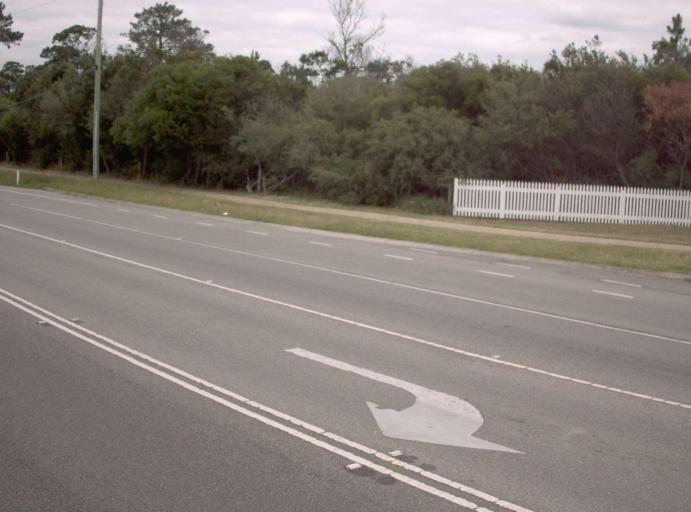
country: AU
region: Victoria
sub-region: Mornington Peninsula
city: Mount Martha
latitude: -38.2562
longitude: 145.0358
